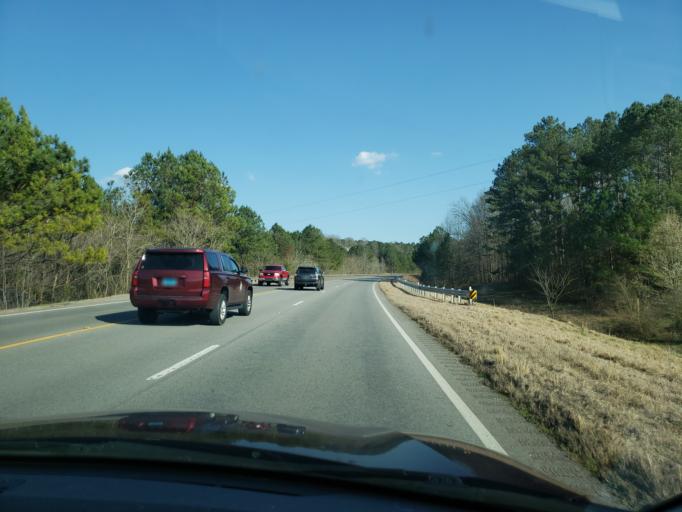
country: US
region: Alabama
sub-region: Cleburne County
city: Heflin
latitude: 33.5031
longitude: -85.6085
